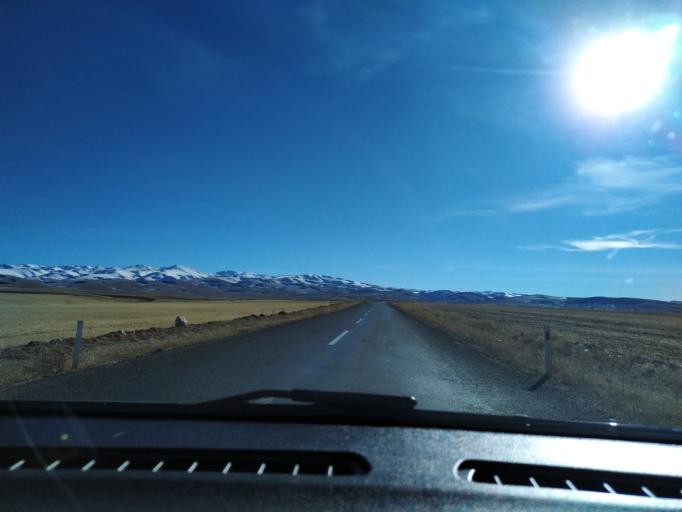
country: TR
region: Kayseri
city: Orensehir
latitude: 38.8916
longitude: 36.7293
